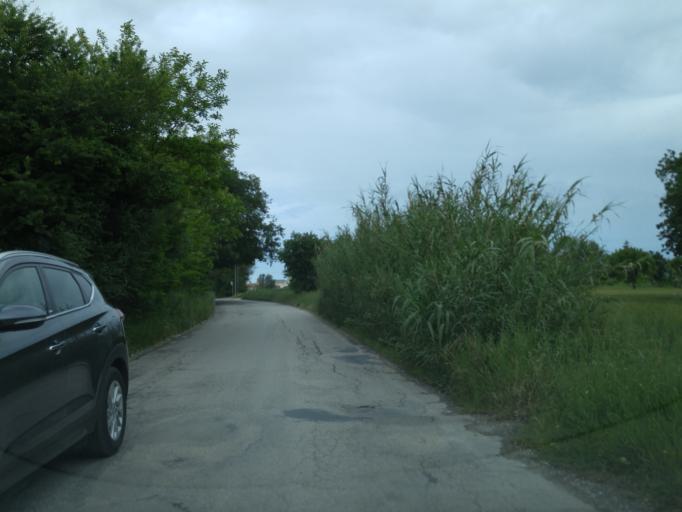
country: IT
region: The Marches
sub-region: Provincia di Pesaro e Urbino
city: Fano
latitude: 43.8274
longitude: 13.0366
